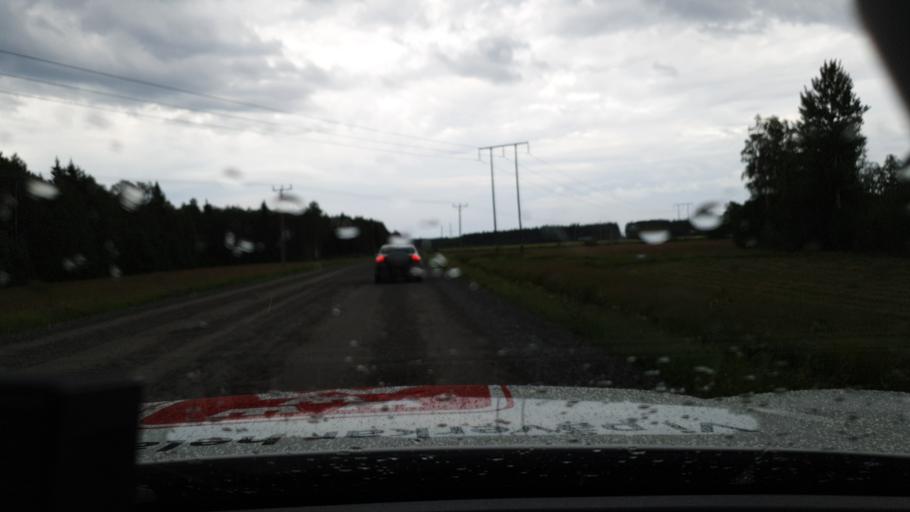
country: SE
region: Norrbotten
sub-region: Bodens Kommun
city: Boden
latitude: 65.8520
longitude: 21.5101
